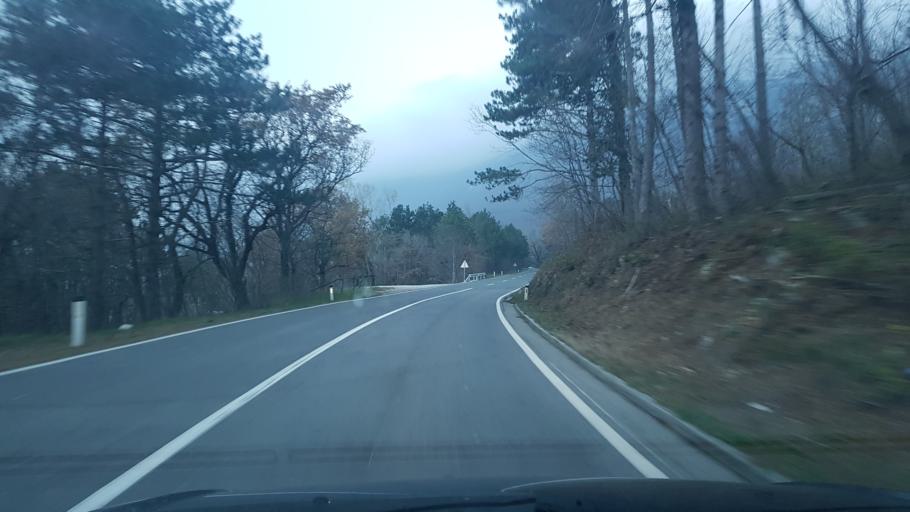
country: SI
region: Ajdovscina
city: Ajdovscina
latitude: 45.8842
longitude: 13.9239
